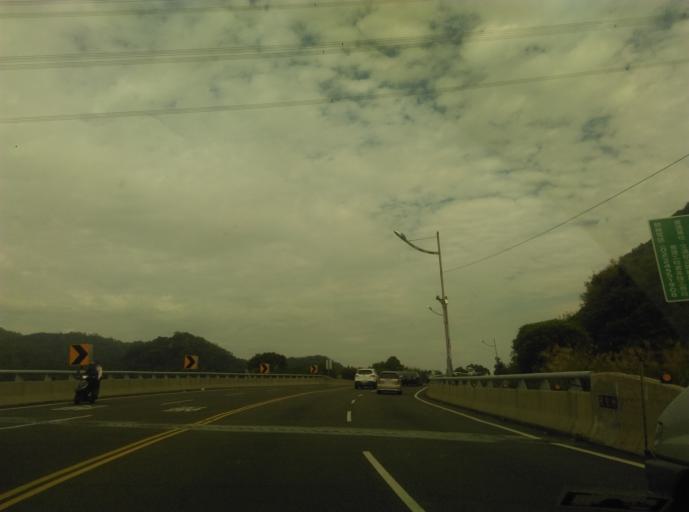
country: TW
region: Taiwan
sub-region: Keelung
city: Keelung
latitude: 25.1589
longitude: 121.6979
